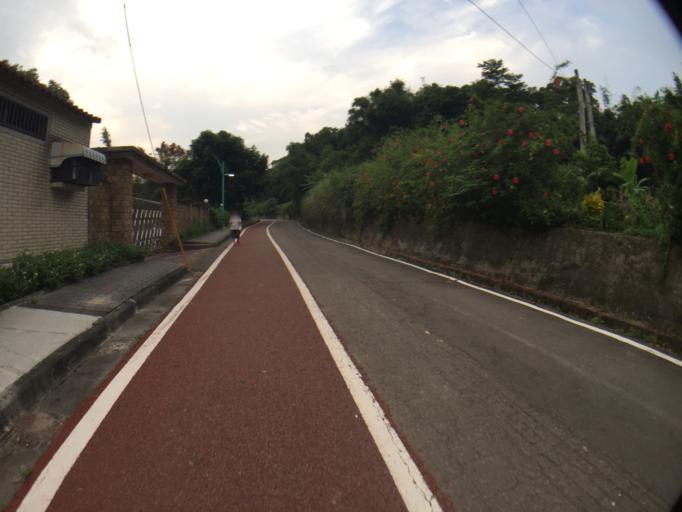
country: TW
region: Taiwan
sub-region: Hsinchu
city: Hsinchu
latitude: 24.7728
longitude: 120.9767
